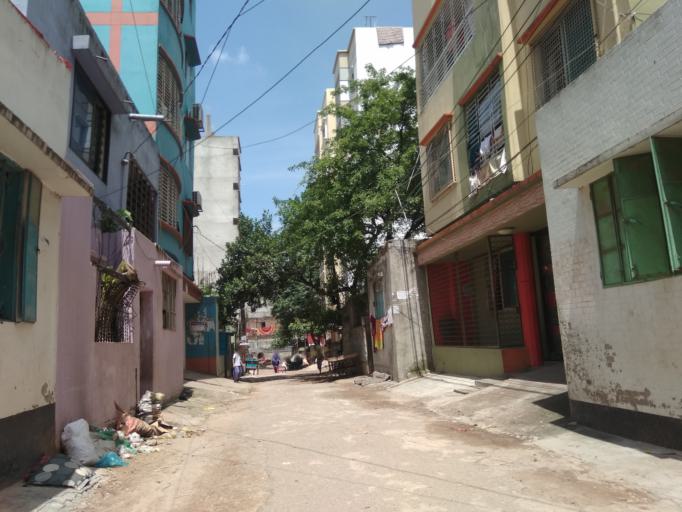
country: BD
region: Dhaka
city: Tungi
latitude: 23.8289
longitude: 90.3754
